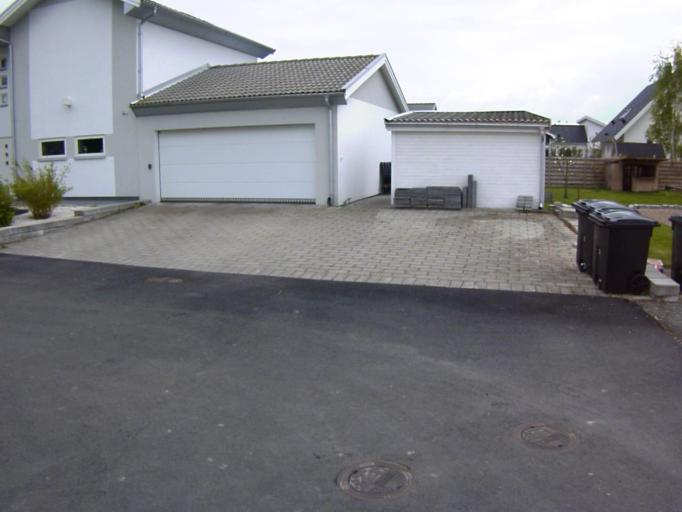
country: SE
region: Skane
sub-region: Kristianstads Kommun
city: Kristianstad
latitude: 56.0182
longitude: 14.1951
